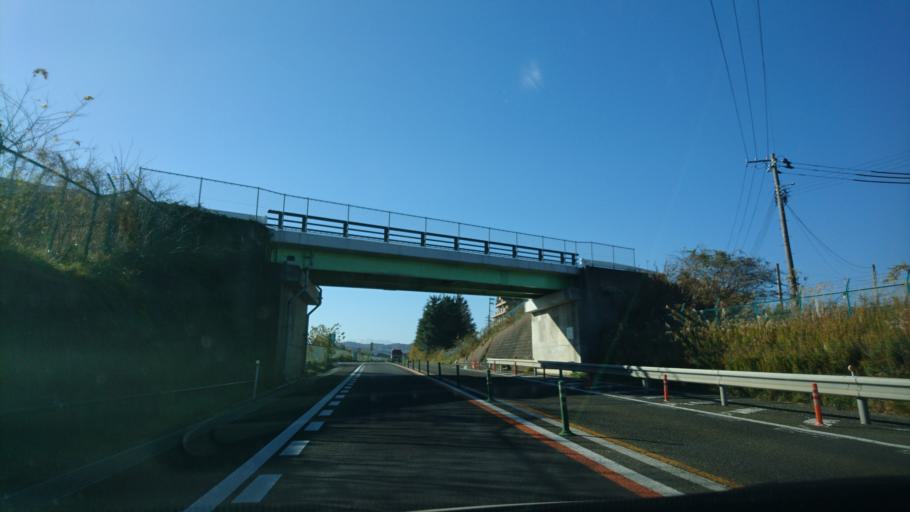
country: JP
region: Miyagi
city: Sendai
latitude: 38.2091
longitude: 140.8916
